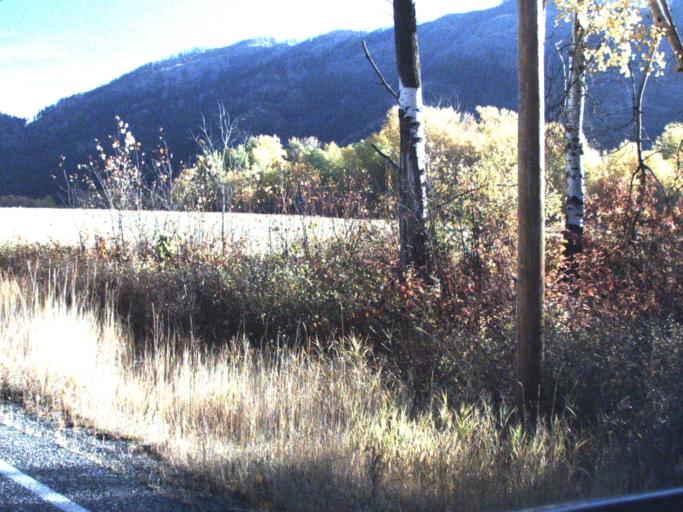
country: US
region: Washington
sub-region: Okanogan County
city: Coulee Dam
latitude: 48.2314
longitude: -118.7010
